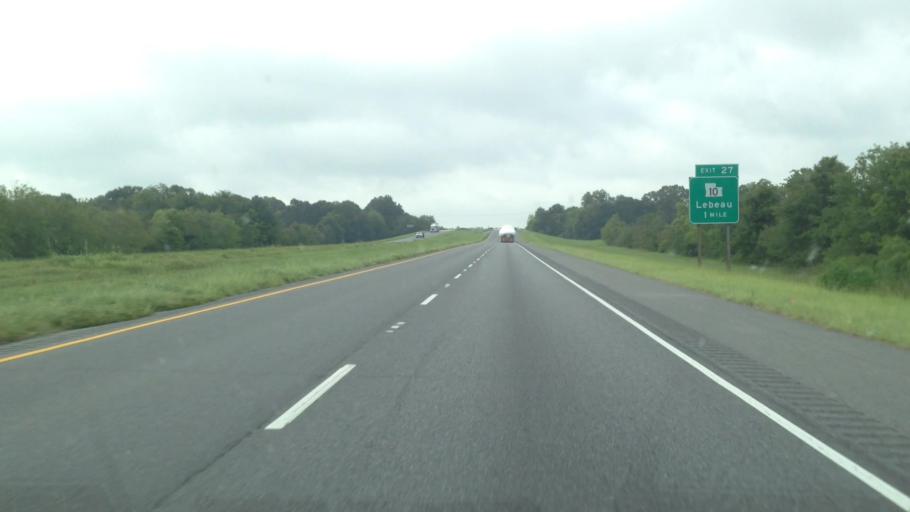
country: US
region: Louisiana
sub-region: Saint Landry Parish
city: Opelousas
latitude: 30.6575
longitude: -92.0633
